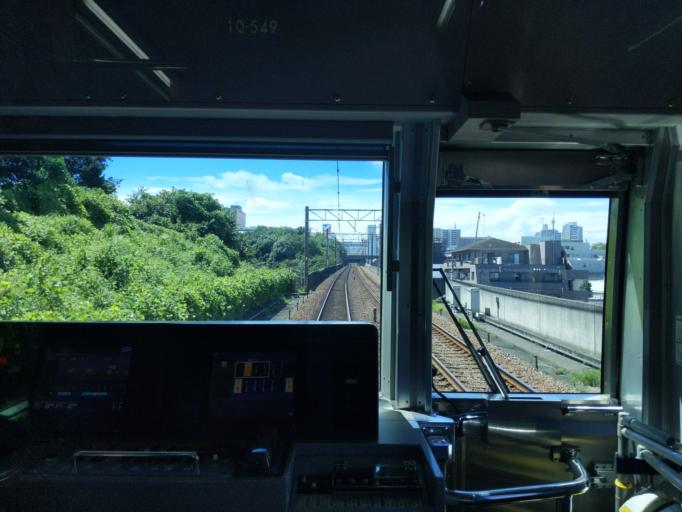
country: JP
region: Tokyo
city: Hino
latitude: 35.6167
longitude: 139.3854
